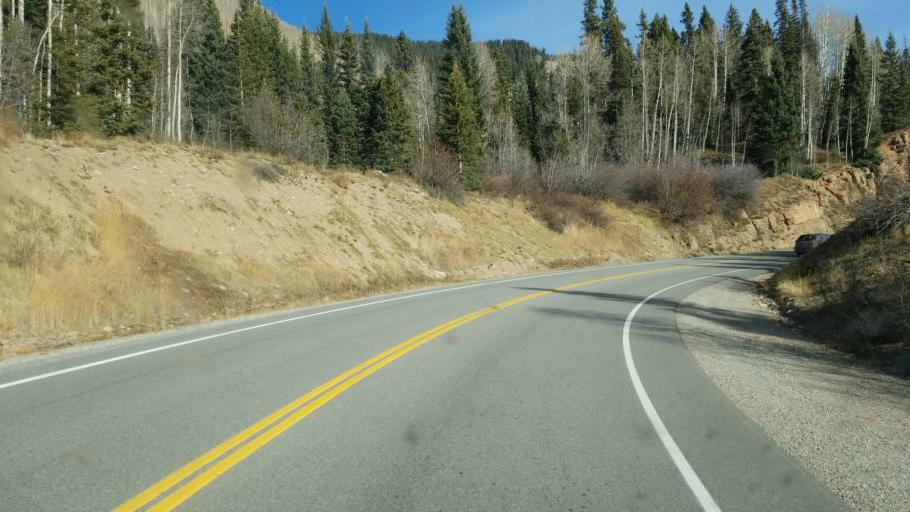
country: US
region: Colorado
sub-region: San Juan County
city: Silverton
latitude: 37.6784
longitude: -107.7961
